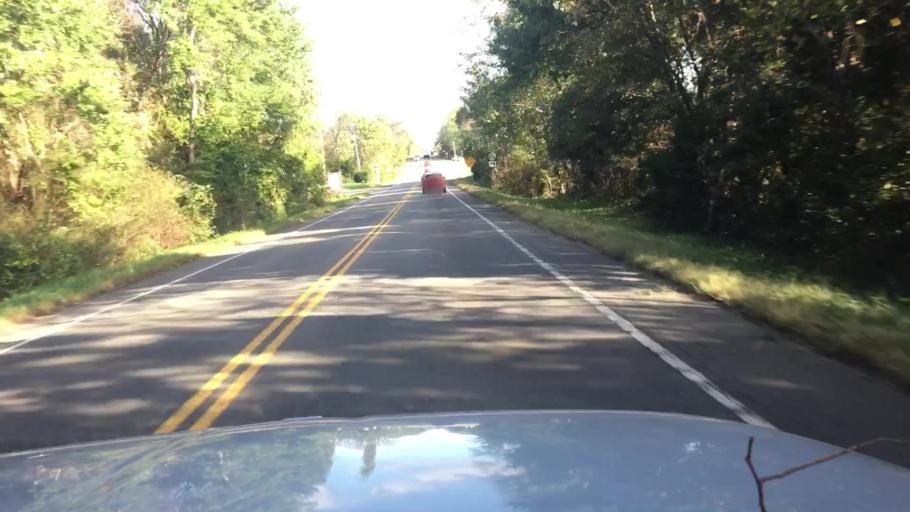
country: US
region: Virginia
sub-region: Prince William County
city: Bull Run Mountain Estates
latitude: 38.9525
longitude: -77.6223
